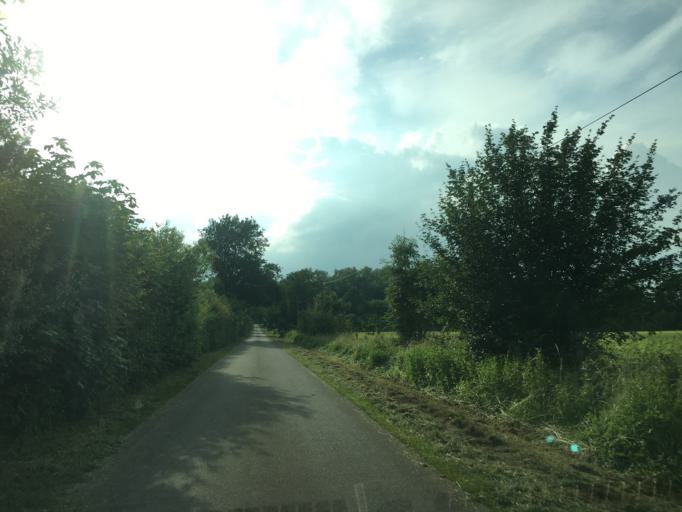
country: DE
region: North Rhine-Westphalia
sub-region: Regierungsbezirk Munster
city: Greven
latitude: 52.0246
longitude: 7.5535
